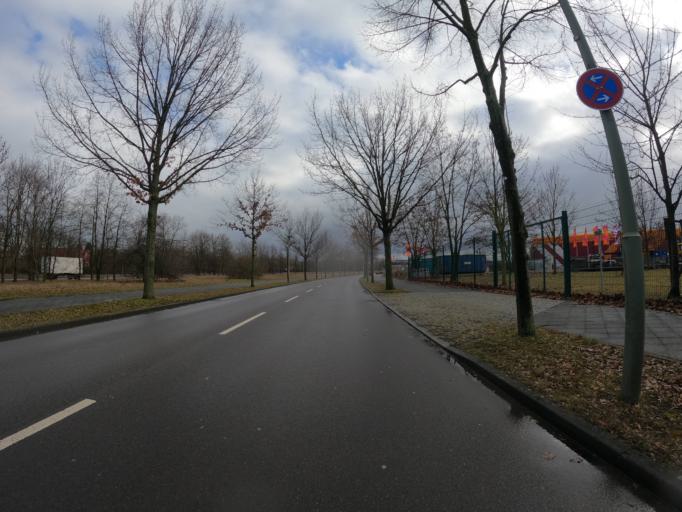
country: DE
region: Berlin
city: Biesdorf
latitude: 52.5194
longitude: 13.5429
